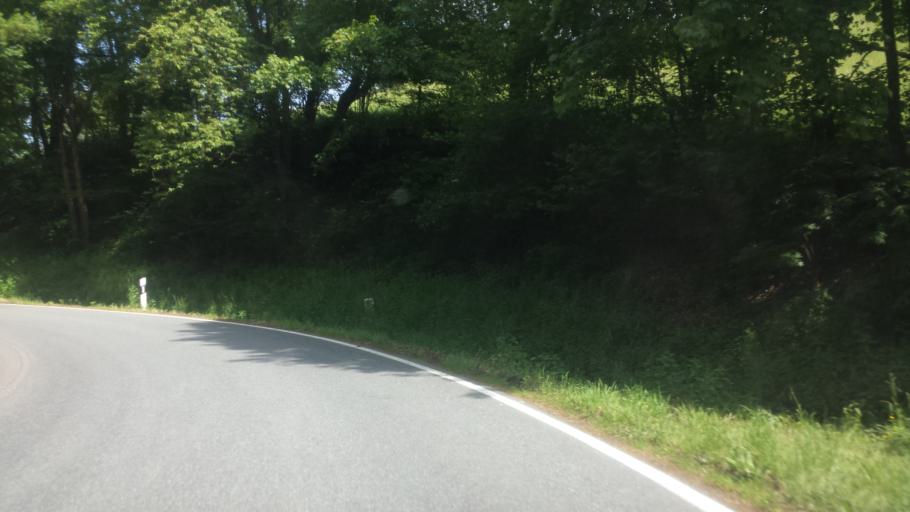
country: DE
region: Hesse
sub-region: Regierungsbezirk Darmstadt
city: Wald-Michelbach
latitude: 49.5759
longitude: 8.8016
